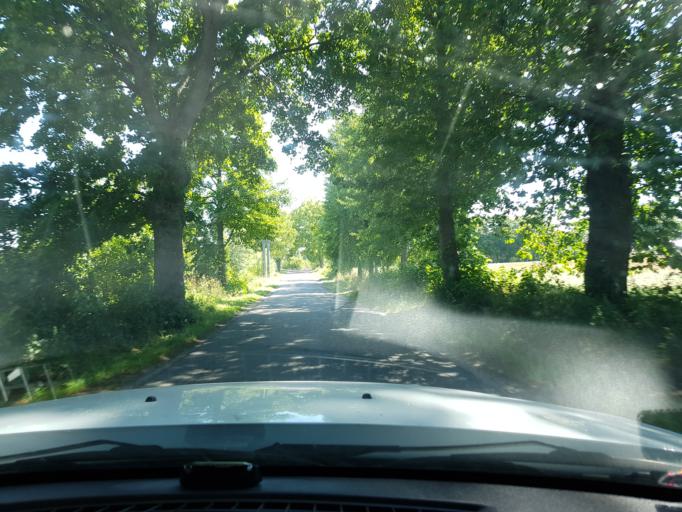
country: PL
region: West Pomeranian Voivodeship
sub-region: Powiat koszalinski
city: Mielno
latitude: 54.1757
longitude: 16.0789
